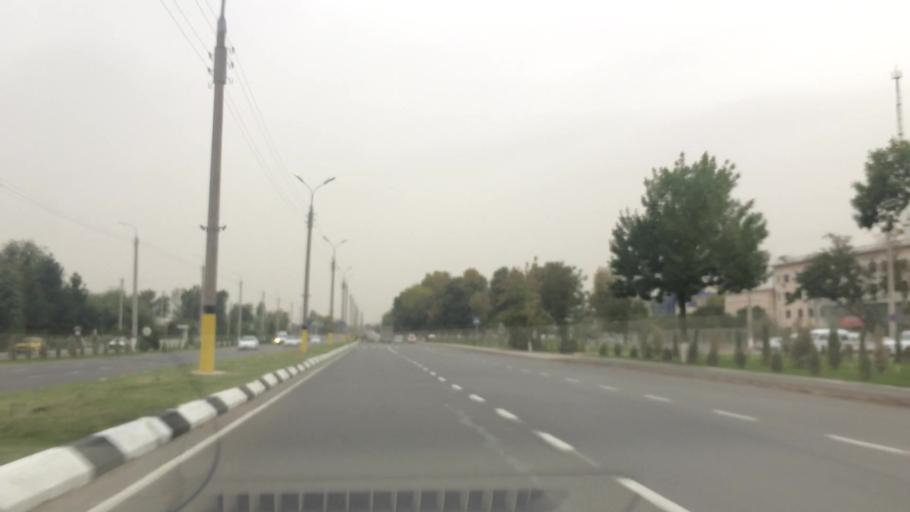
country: UZ
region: Toshkent
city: Salor
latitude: 41.3150
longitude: 69.3529
